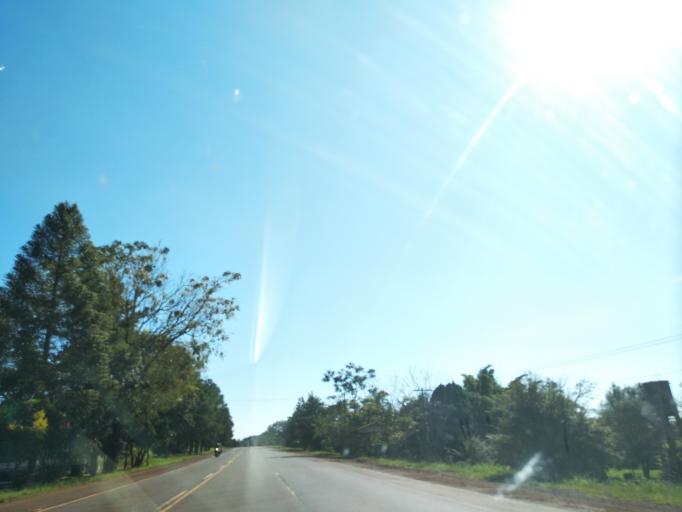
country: AR
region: Misiones
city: Garuhape
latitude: -26.8217
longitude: -54.9713
